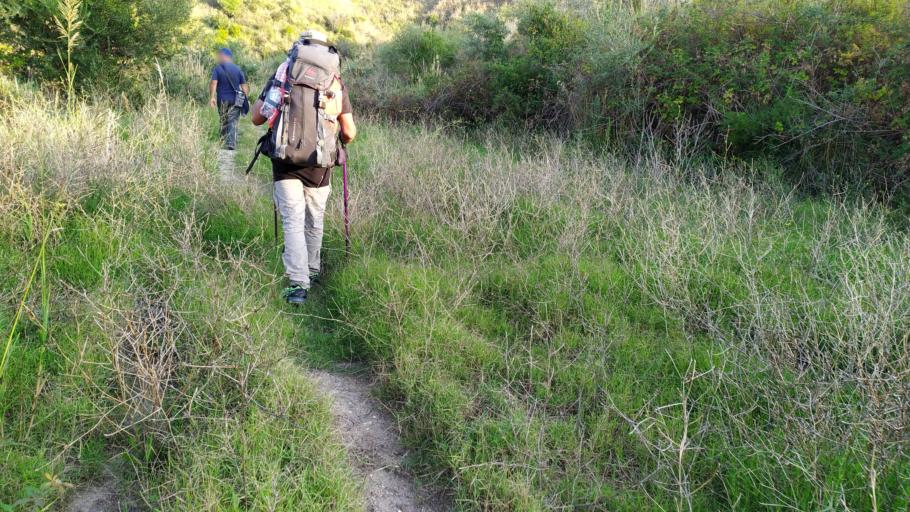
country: IT
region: Sicily
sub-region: Messina
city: Saponara Marittima
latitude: 38.2250
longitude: 15.4314
